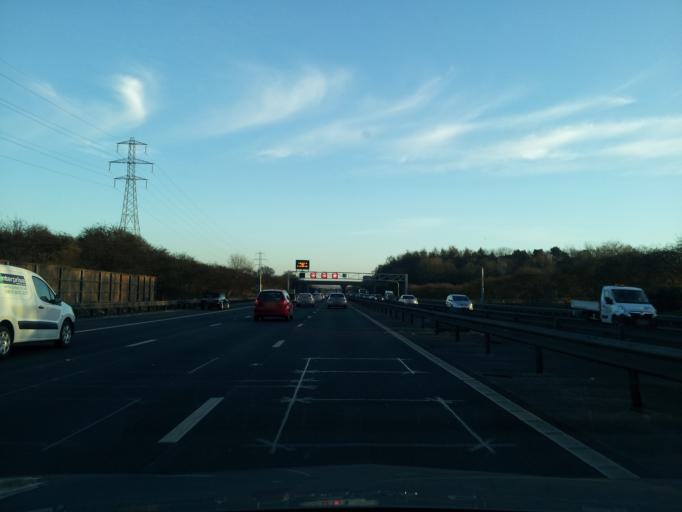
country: GB
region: England
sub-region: Central Bedfordshire
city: Steppingley
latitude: 52.0017
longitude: -0.5442
